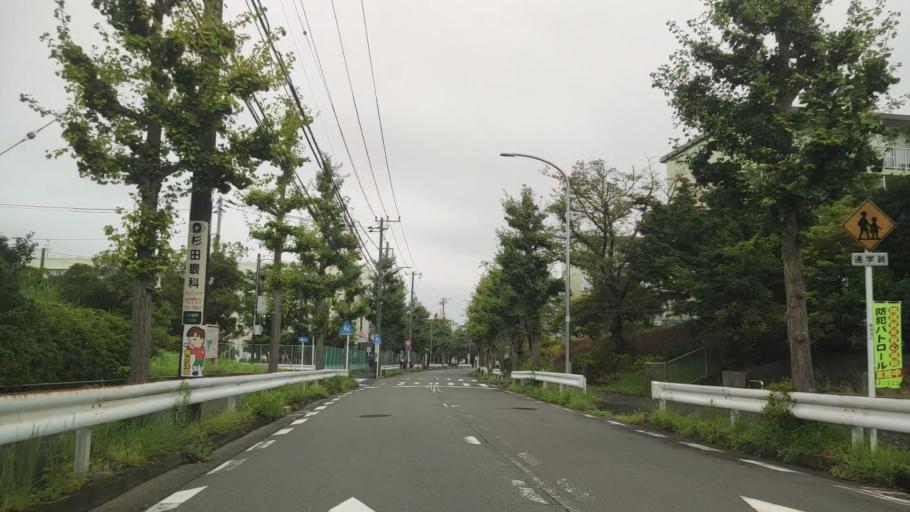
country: JP
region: Kanagawa
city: Zushi
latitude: 35.3680
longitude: 139.6092
